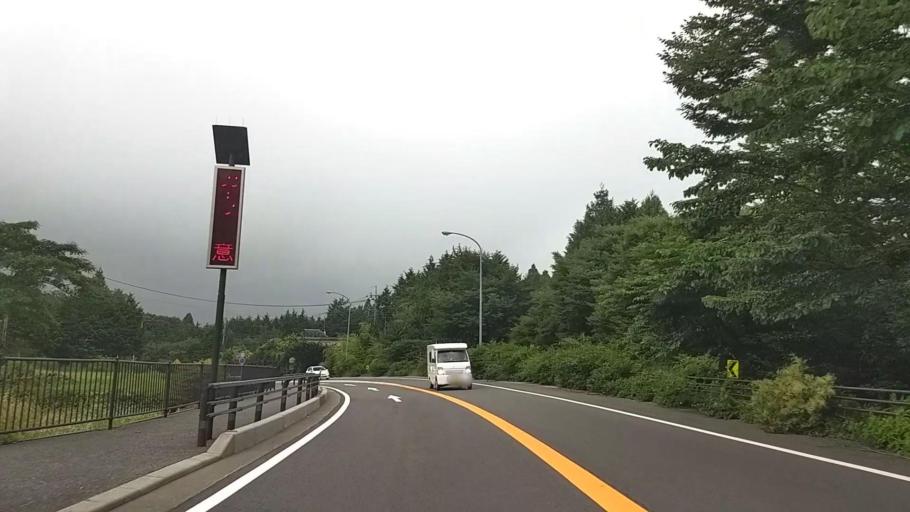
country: JP
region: Yamanashi
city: Fujikawaguchiko
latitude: 35.4278
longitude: 138.5903
